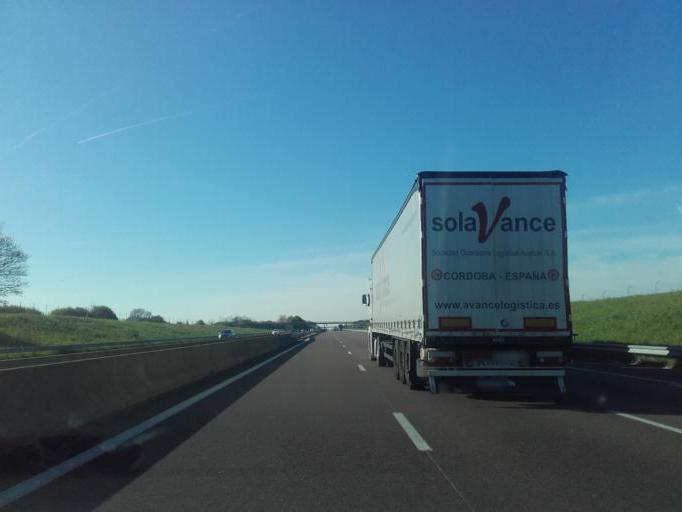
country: FR
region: Bourgogne
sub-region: Departement de Saone-et-Loire
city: Sevrey
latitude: 46.7462
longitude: 4.8330
